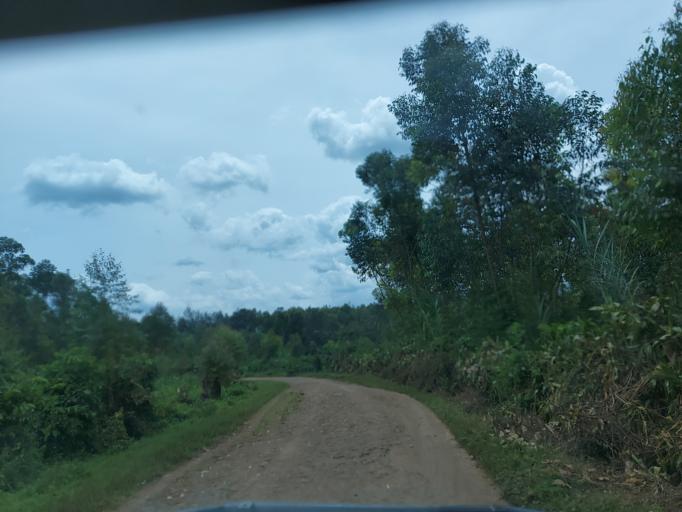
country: CD
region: South Kivu
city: Bukavu
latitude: -2.2450
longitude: 28.8222
